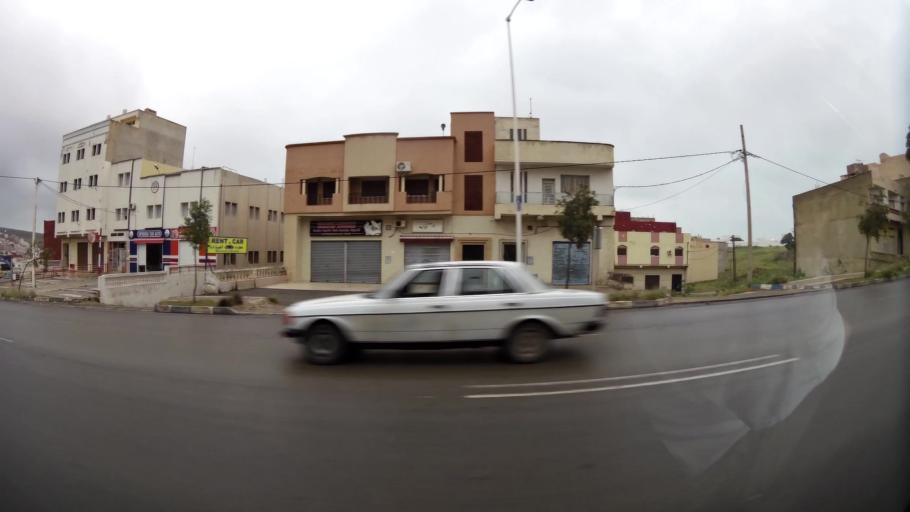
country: MA
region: Oriental
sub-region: Nador
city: Nador
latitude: 35.1899
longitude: -2.9310
